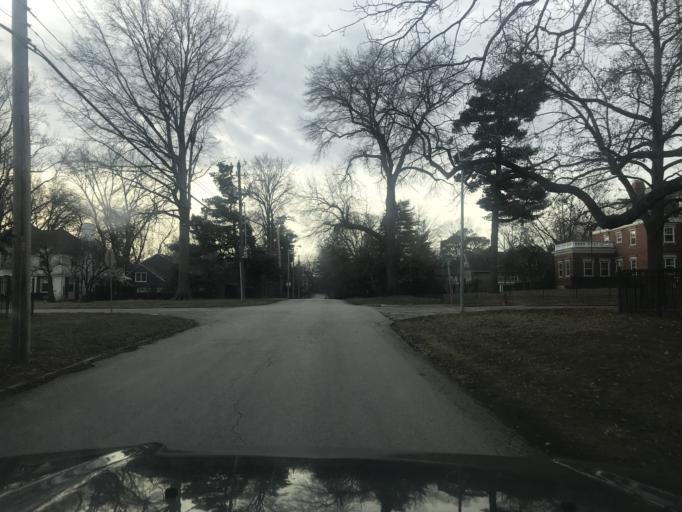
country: US
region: Kansas
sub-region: Johnson County
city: Westwood
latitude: 39.0298
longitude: -94.5995
